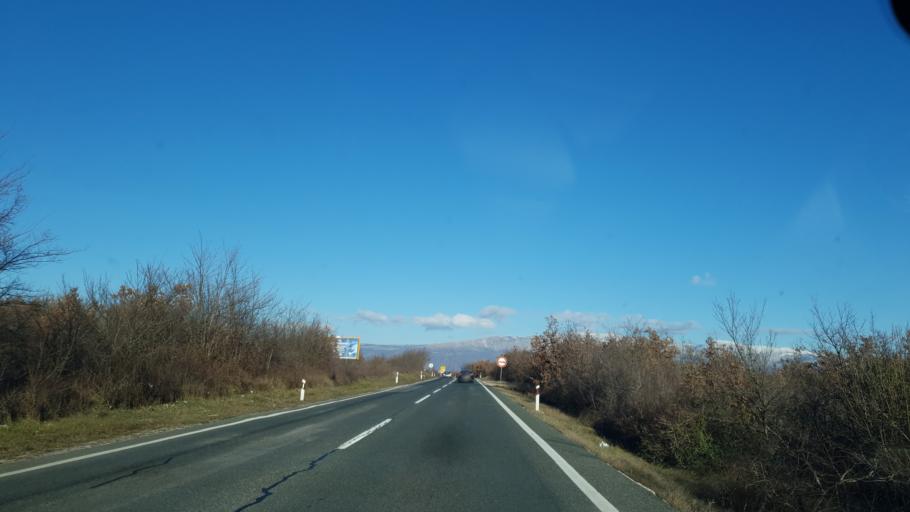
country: HR
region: Splitsko-Dalmatinska
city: Brnaze
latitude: 43.6496
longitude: 16.6338
